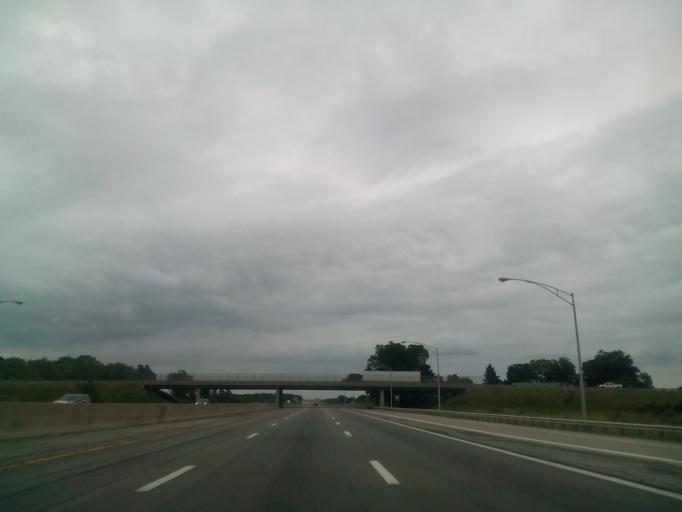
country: US
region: Ohio
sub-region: Huron County
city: Bellevue
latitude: 41.3404
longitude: -82.7617
